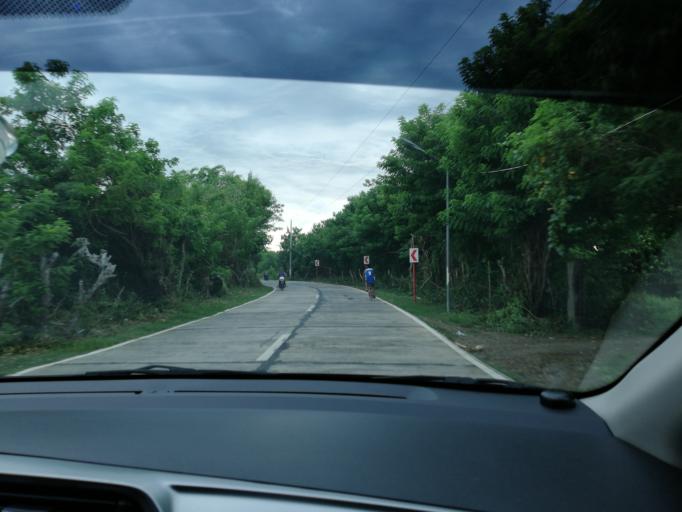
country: PH
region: Ilocos
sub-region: Province of Ilocos Sur
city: Narvacan
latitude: 17.4184
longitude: 120.4596
